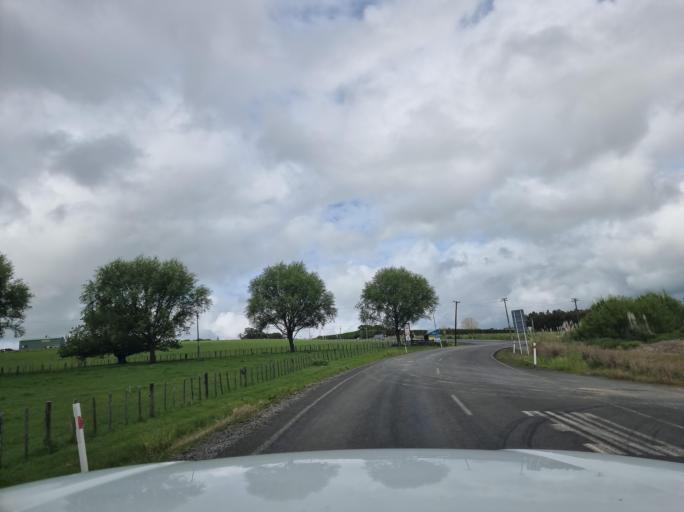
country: NZ
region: Northland
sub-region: Whangarei
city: Ruakaka
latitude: -36.1250
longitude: 174.1887
